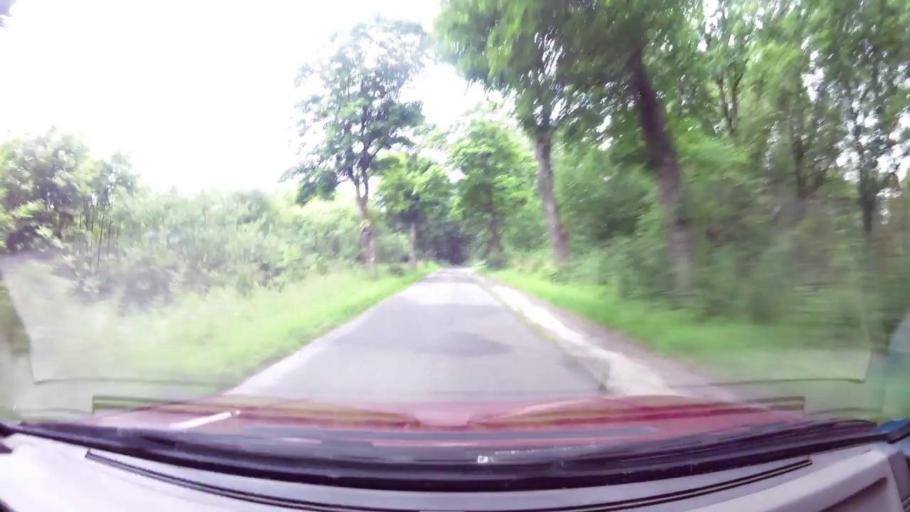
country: PL
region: West Pomeranian Voivodeship
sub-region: Powiat swidwinski
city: Rabino
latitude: 53.9237
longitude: 15.9607
